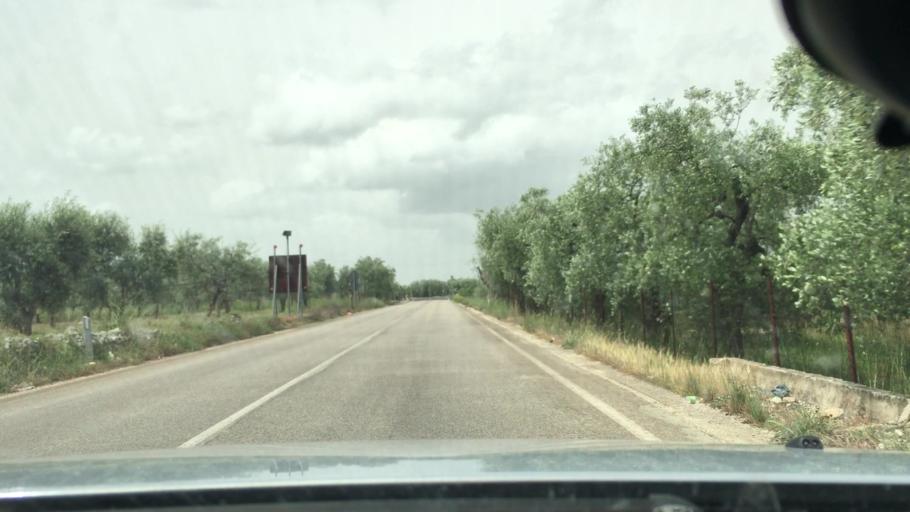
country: IT
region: Apulia
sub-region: Provincia di Bari
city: Capurso
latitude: 41.0410
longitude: 16.9482
